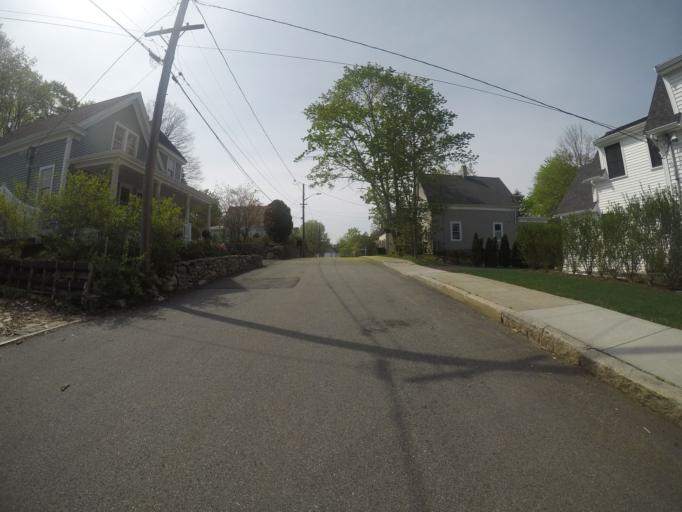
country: US
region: Massachusetts
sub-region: Bristol County
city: Easton
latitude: 42.0678
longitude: -71.1012
